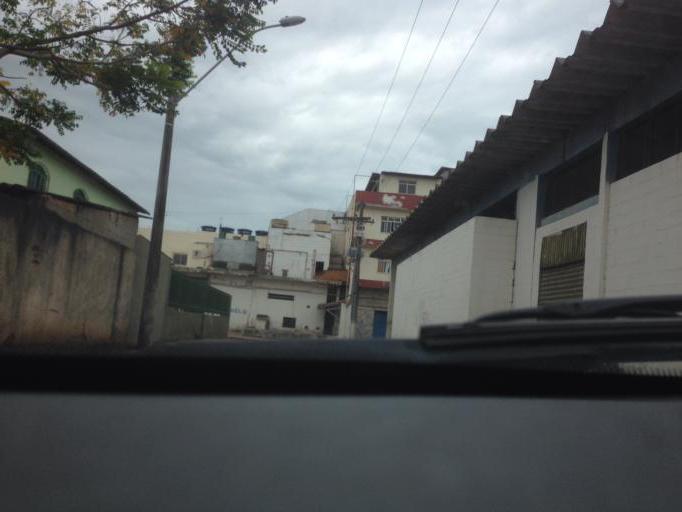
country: BR
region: Espirito Santo
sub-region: Guarapari
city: Guarapari
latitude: -20.6705
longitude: -40.5018
